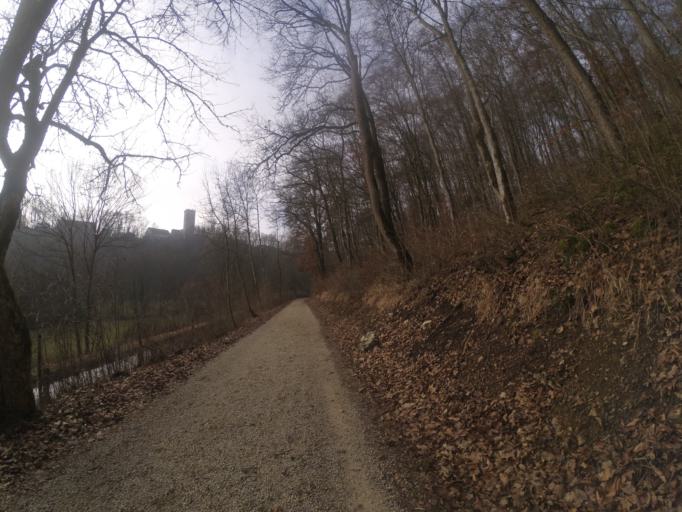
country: DE
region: Baden-Wuerttemberg
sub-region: Tuebingen Region
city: Lauterach
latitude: 48.2611
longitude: 9.5593
